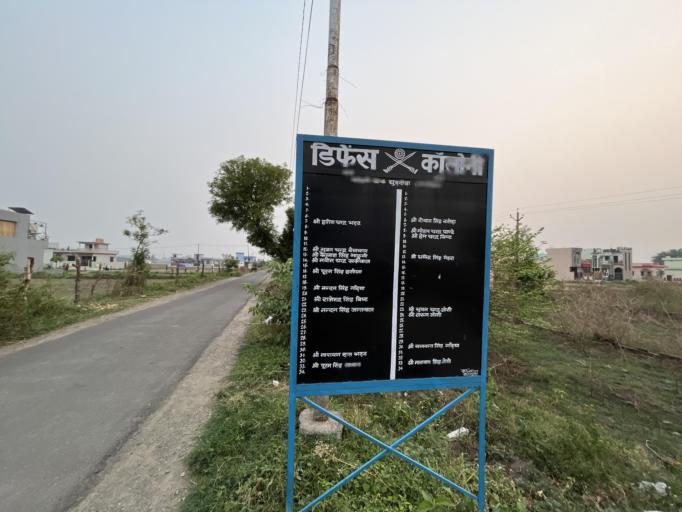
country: IN
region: Uttarakhand
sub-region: Naini Tal
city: Haldwani
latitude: 29.1655
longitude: 79.4790
